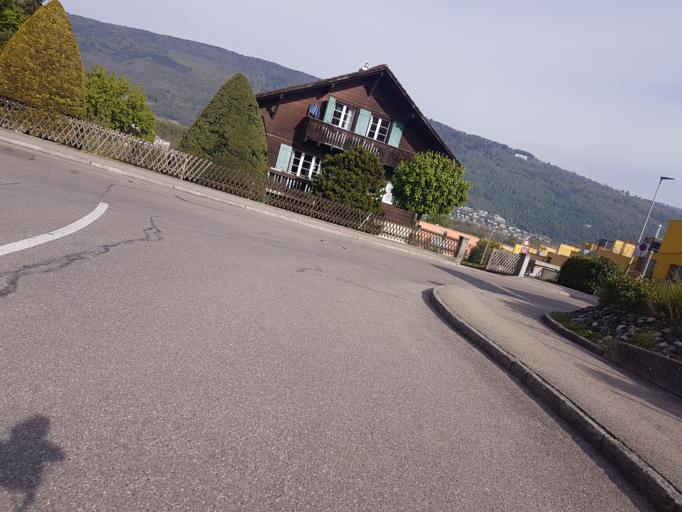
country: CH
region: Bern
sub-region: Biel/Bienne District
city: Bellmund
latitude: 47.1131
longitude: 7.2340
